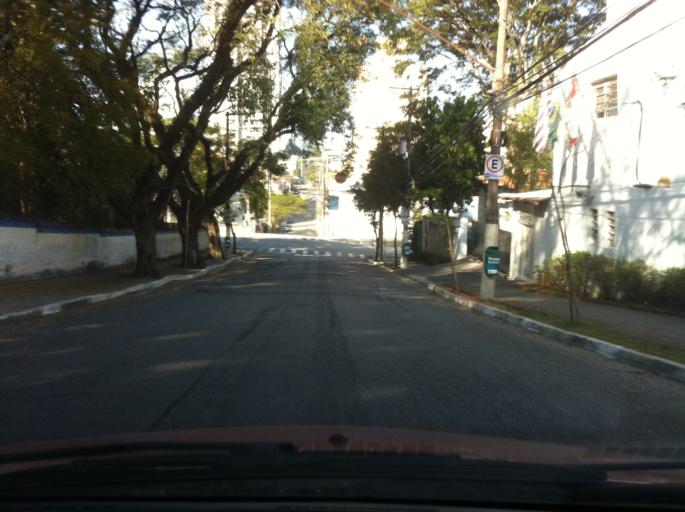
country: BR
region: Sao Paulo
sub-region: Sao Paulo
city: Sao Paulo
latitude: -23.5983
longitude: -46.6493
